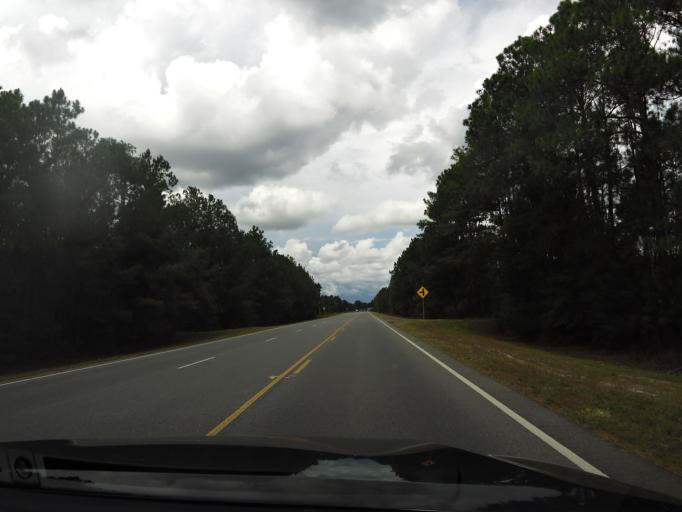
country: US
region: Georgia
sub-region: Brantley County
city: Nahunta
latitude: 31.1843
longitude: -81.9872
